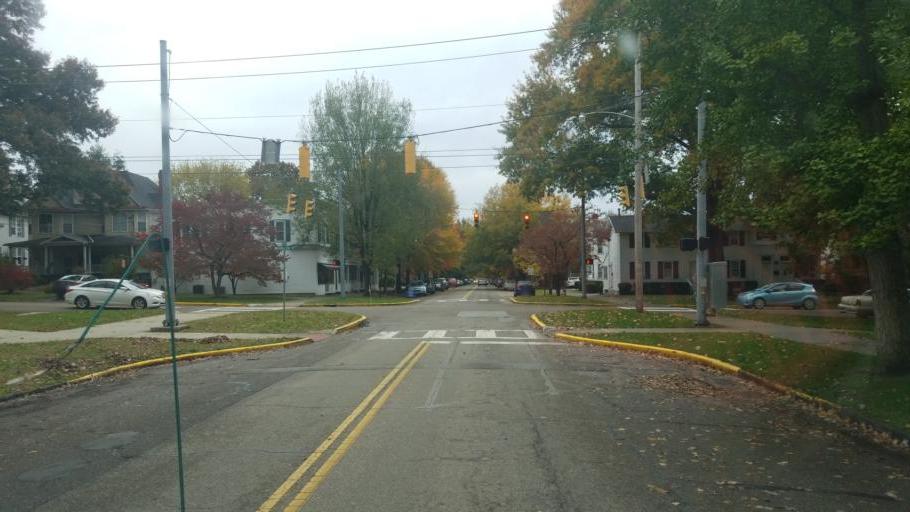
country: US
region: Ohio
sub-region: Washington County
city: Marietta
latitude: 39.4232
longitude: -81.4583
